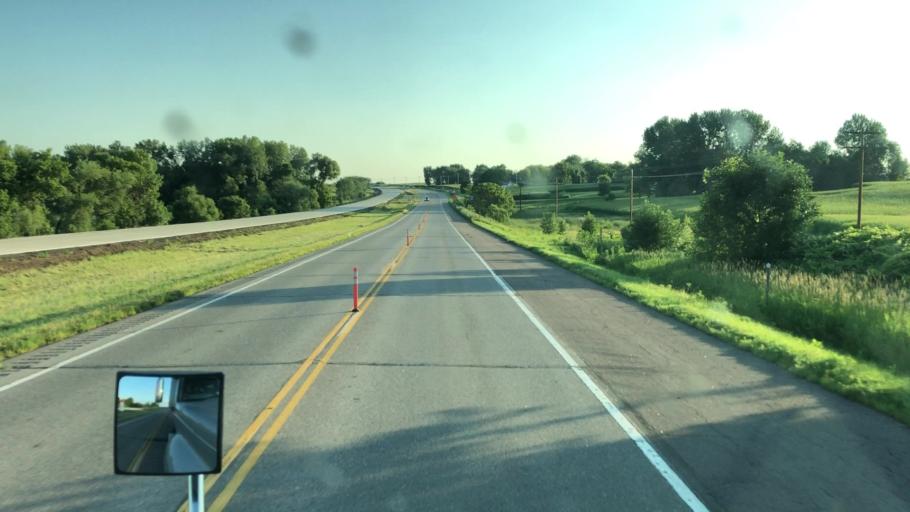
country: US
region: Minnesota
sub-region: Scott County
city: Belle Plaine
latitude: 44.5894
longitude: -93.8239
